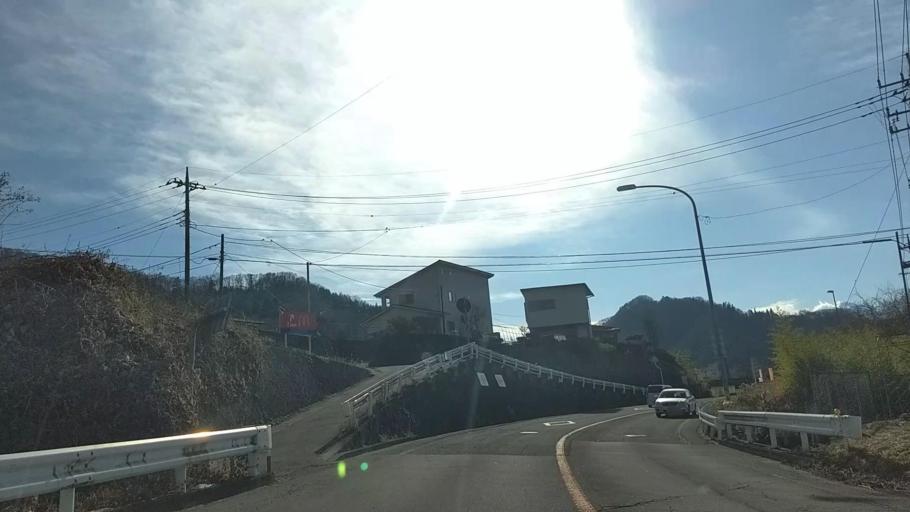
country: JP
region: Yamanashi
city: Otsuki
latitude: 35.5794
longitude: 138.9358
